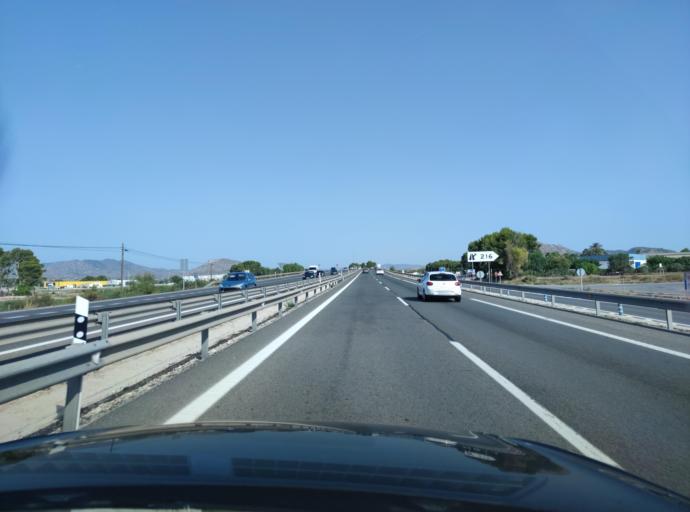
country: ES
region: Valencia
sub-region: Provincia de Alicante
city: Monforte del Cid
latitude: 38.3904
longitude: -0.7417
